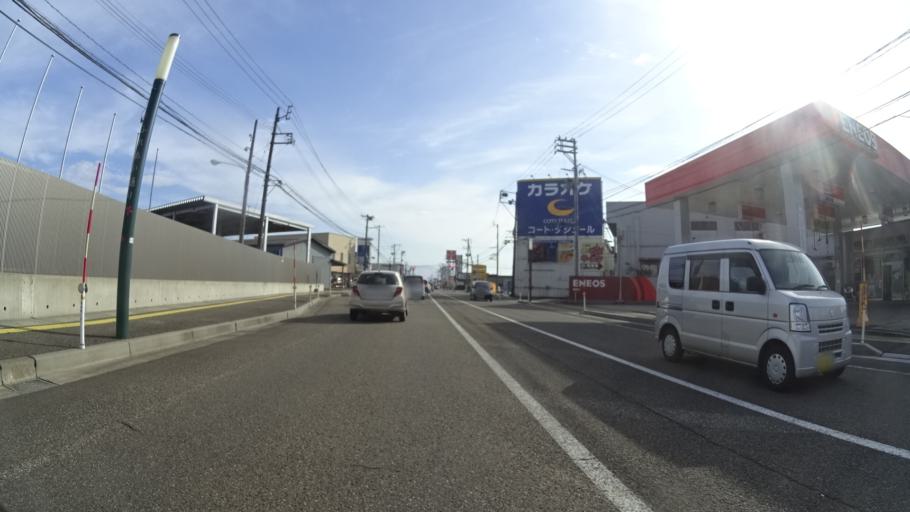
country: JP
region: Niigata
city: Joetsu
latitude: 37.1305
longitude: 138.2457
